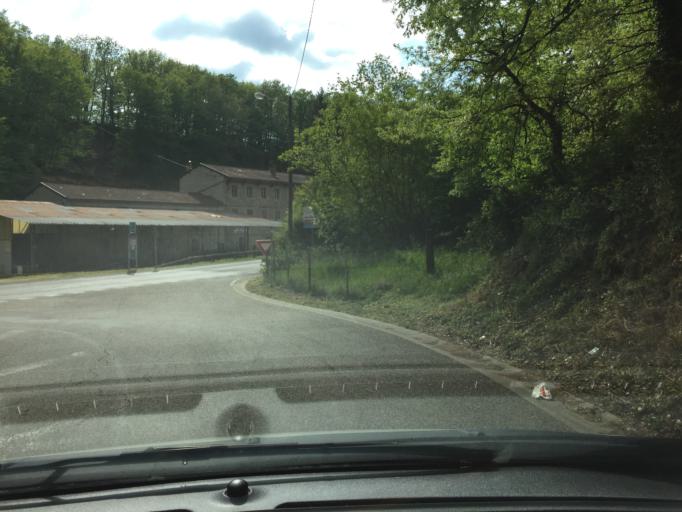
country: FR
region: Rhone-Alpes
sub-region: Departement du Rhone
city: Orlienas
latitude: 45.6629
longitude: 4.7134
